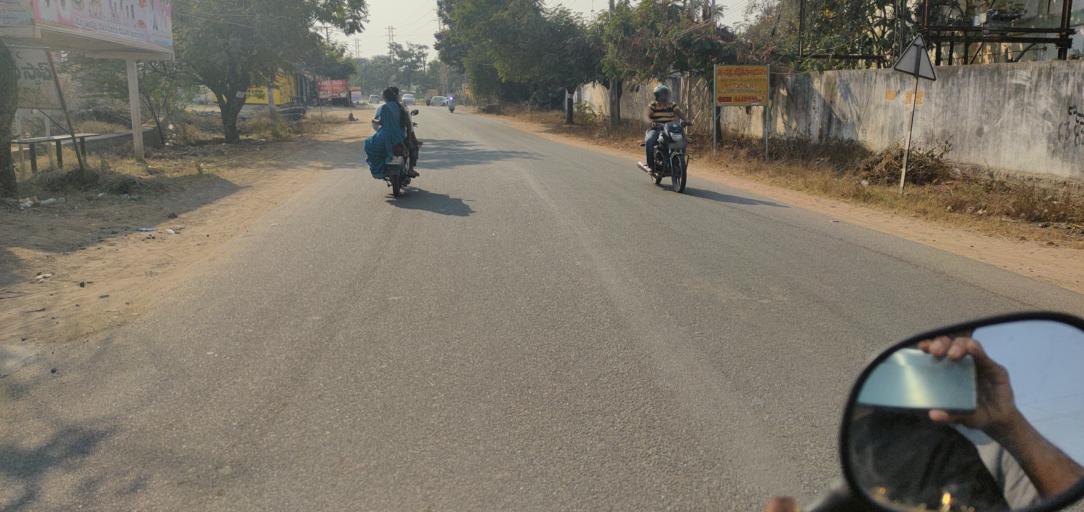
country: IN
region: Telangana
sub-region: Rangareddi
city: Lal Bahadur Nagar
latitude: 17.3389
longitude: 78.6224
